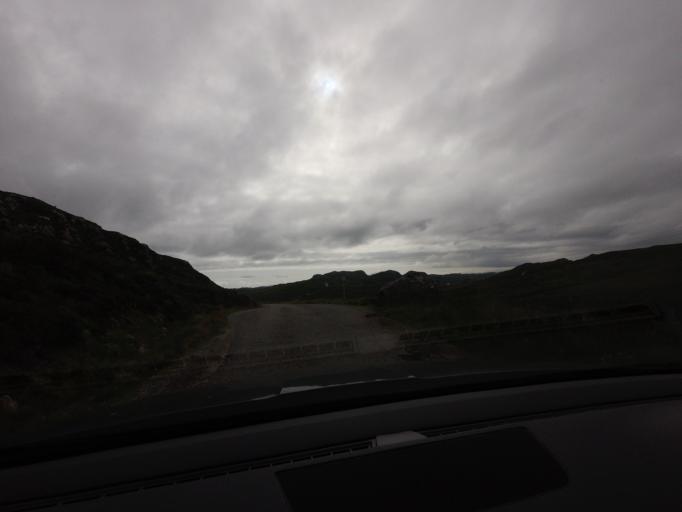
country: GB
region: Scotland
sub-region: Highland
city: Ullapool
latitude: 58.4411
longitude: -4.9566
